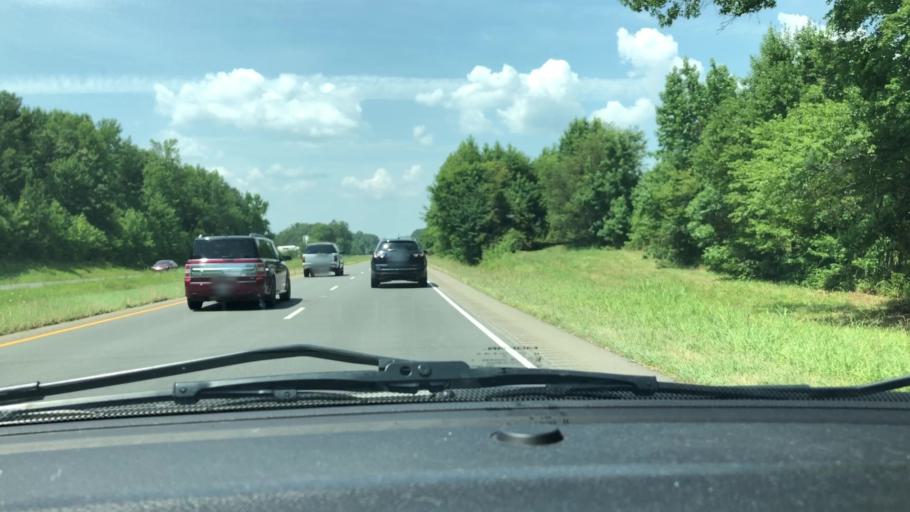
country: US
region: North Carolina
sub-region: Chatham County
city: Siler City
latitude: 35.6703
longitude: -79.4107
